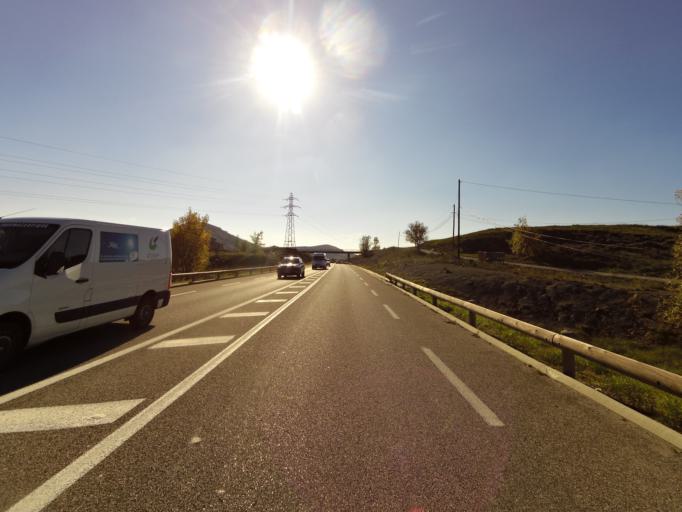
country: FR
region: Rhone-Alpes
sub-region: Departement de l'Ardeche
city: Saint-Sernin
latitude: 44.5812
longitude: 4.3827
